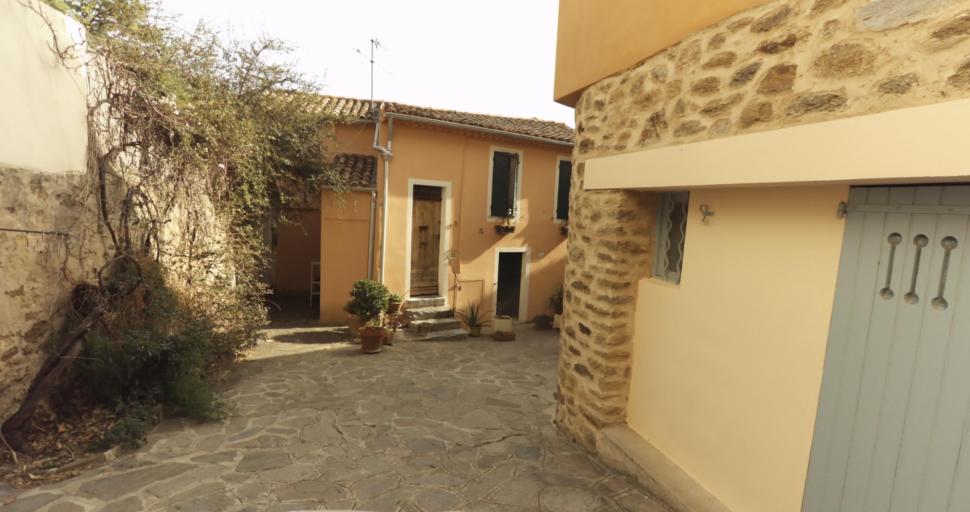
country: FR
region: Provence-Alpes-Cote d'Azur
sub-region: Departement du Var
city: Bormes-les-Mimosas
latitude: 43.1513
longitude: 6.3430
